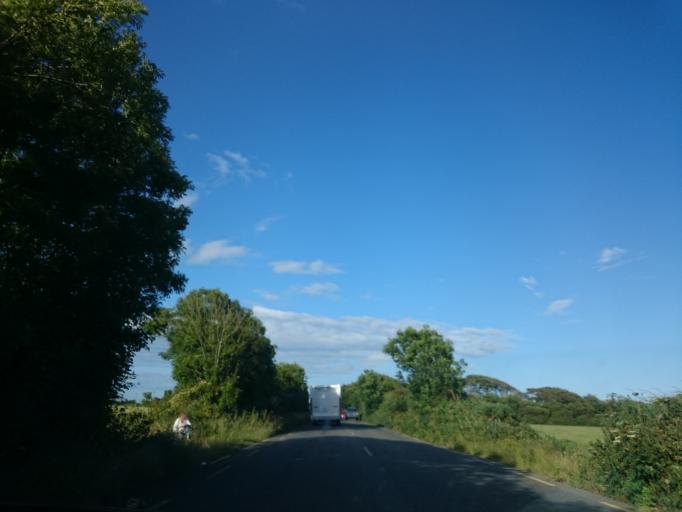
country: IE
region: Leinster
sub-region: Loch Garman
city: Loch Garman
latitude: 52.2088
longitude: -6.5395
